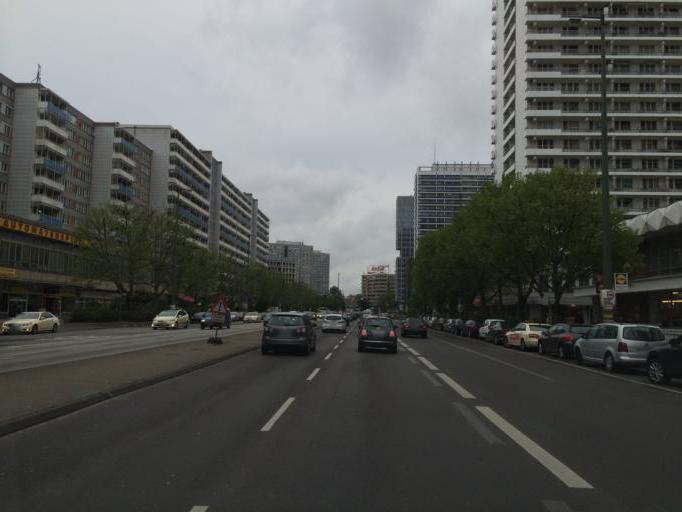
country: DE
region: Berlin
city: Mitte
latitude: 52.5109
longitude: 13.3960
